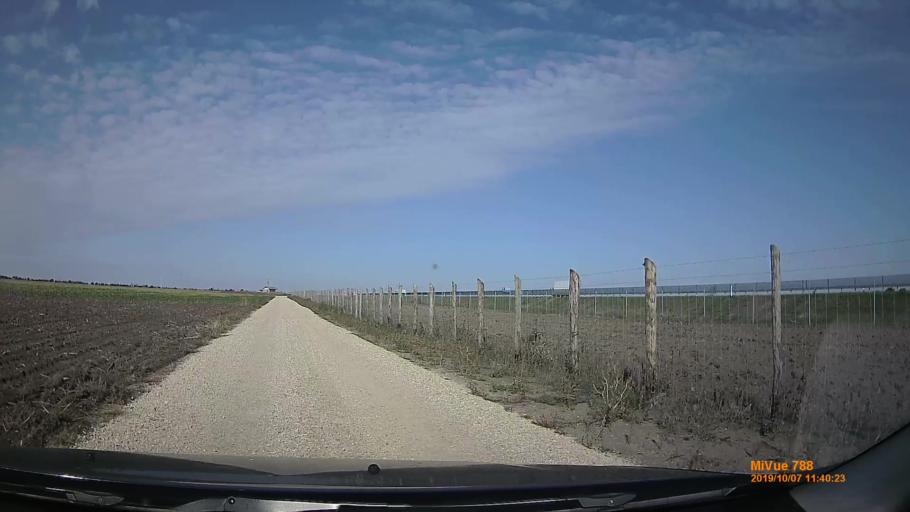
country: HU
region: Bekes
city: Kondoros
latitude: 46.7884
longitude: 20.7095
